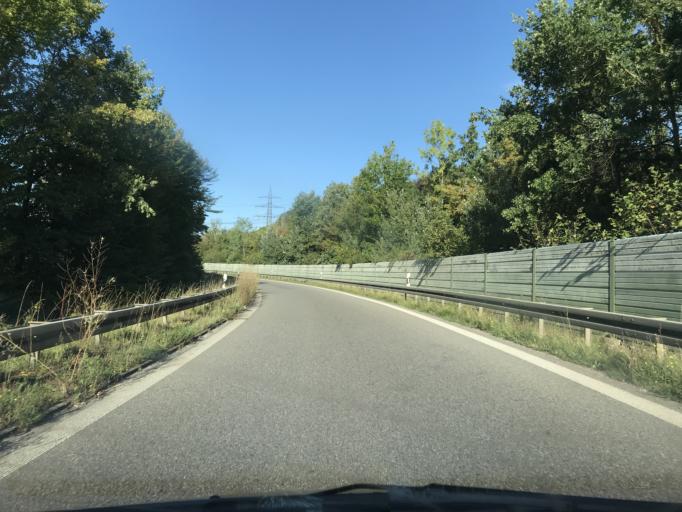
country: DE
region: Baden-Wuerttemberg
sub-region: Freiburg Region
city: Loerrach
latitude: 47.6341
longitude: 7.6730
